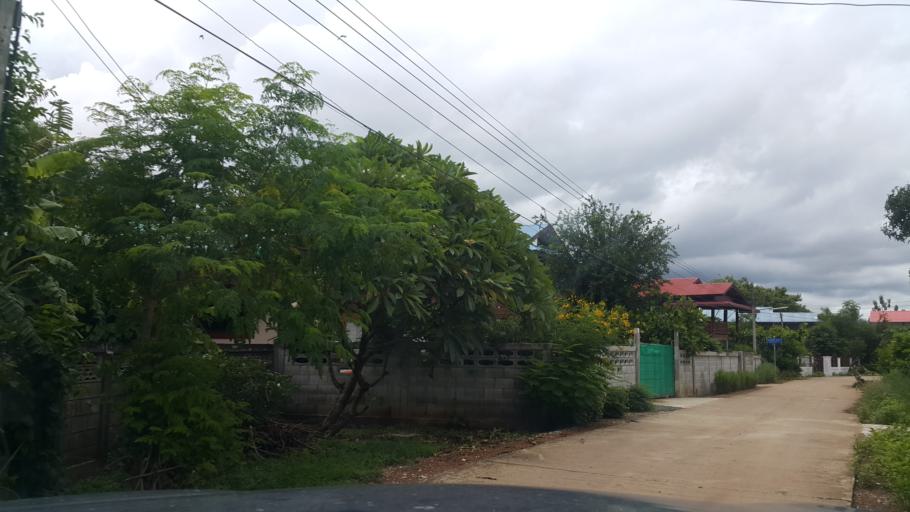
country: TH
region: Sukhothai
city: Thung Saliam
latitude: 17.3179
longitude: 99.5781
